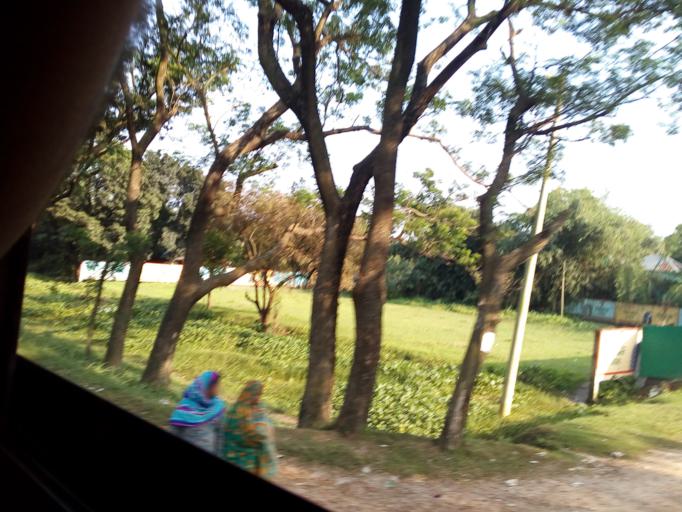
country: BD
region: Dhaka
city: Mirzapur
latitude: 23.9212
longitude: 90.1329
